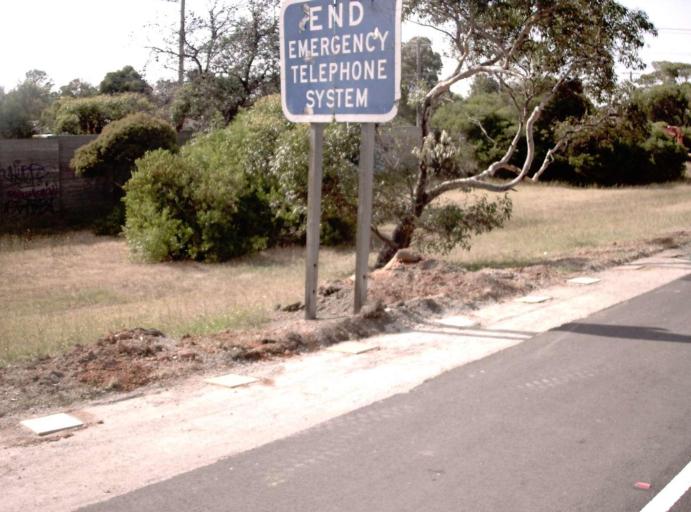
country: AU
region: Victoria
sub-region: Casey
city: Hampton Park
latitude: -38.0287
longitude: 145.2470
